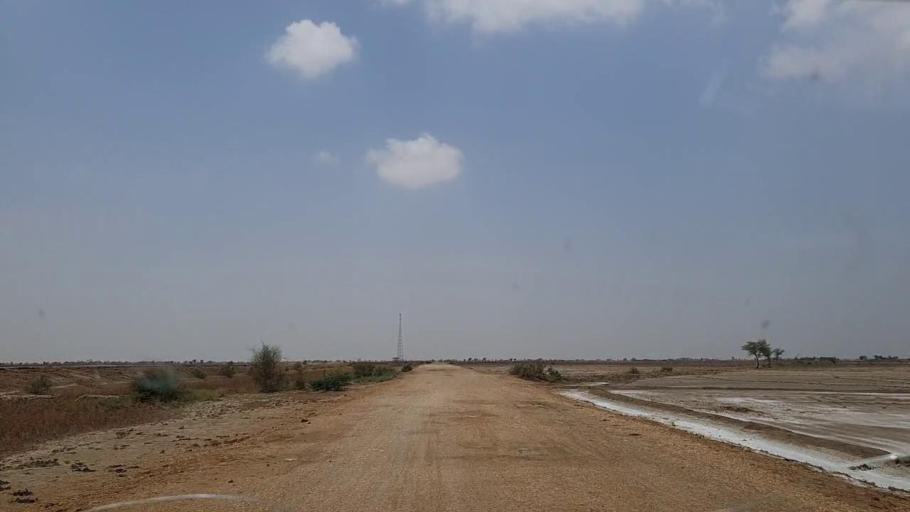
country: PK
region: Sindh
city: Johi
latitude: 26.7798
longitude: 67.6507
